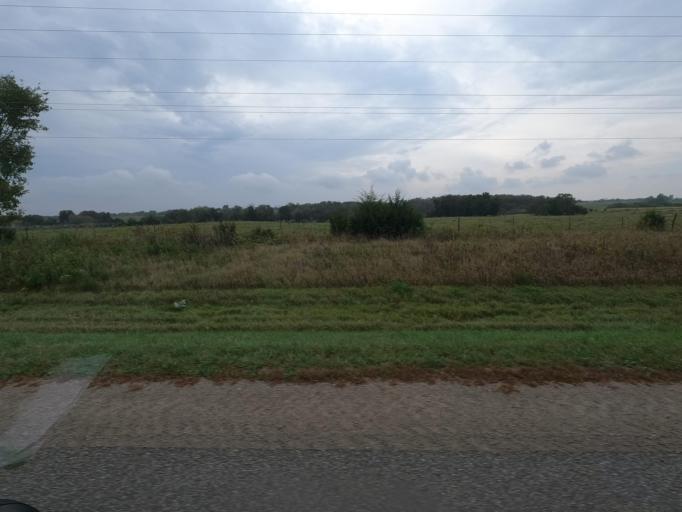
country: US
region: Iowa
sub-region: Van Buren County
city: Keosauqua
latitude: 40.8125
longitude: -91.9368
